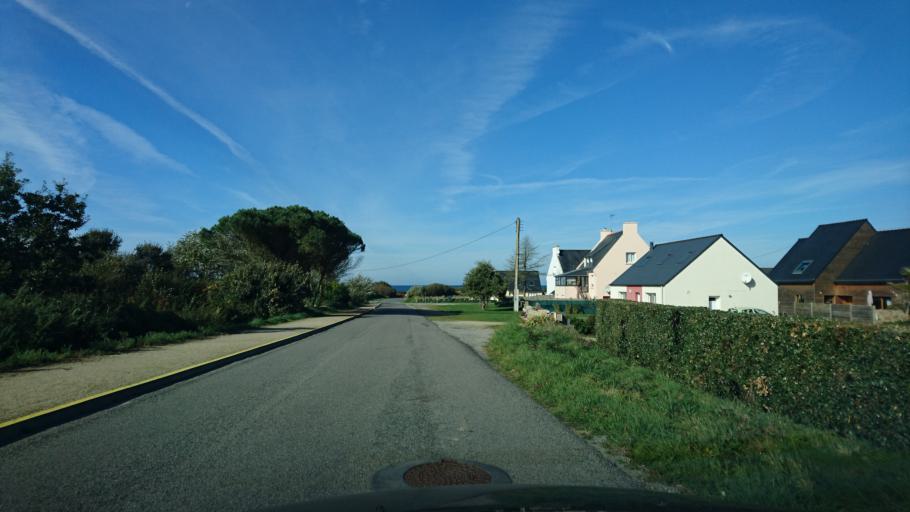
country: FR
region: Brittany
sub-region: Departement du Finistere
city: Lampaul-Plouarzel
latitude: 48.4368
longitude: -4.7782
